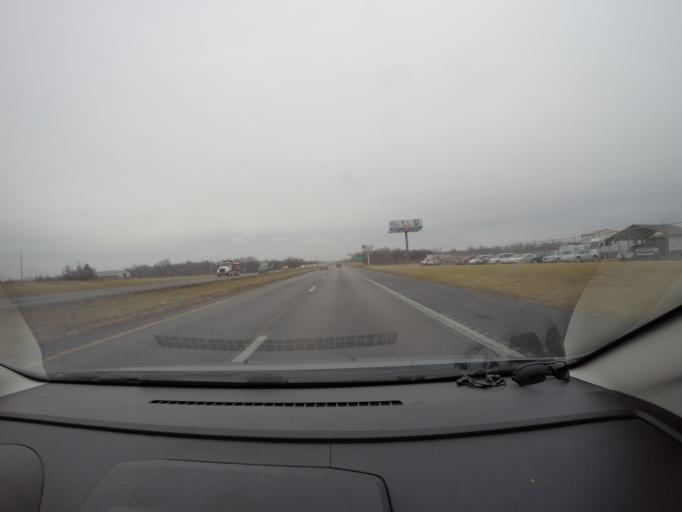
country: US
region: Missouri
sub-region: Gasconade County
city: Hermann
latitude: 38.8656
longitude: -91.3300
